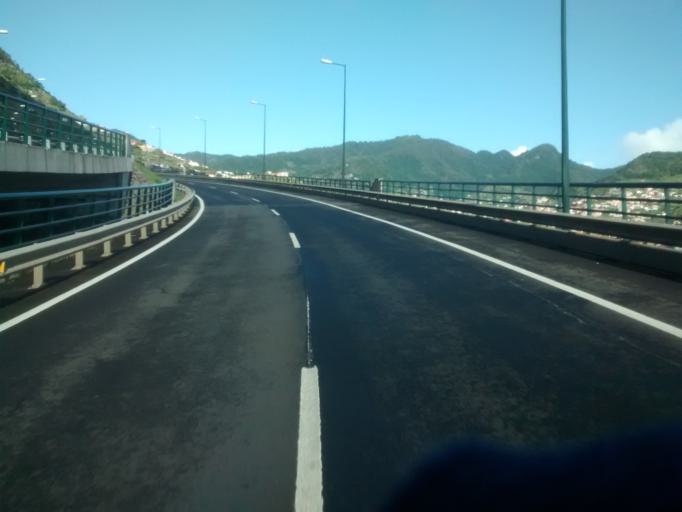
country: PT
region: Madeira
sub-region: Machico
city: Machico
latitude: 32.7162
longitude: -16.7682
